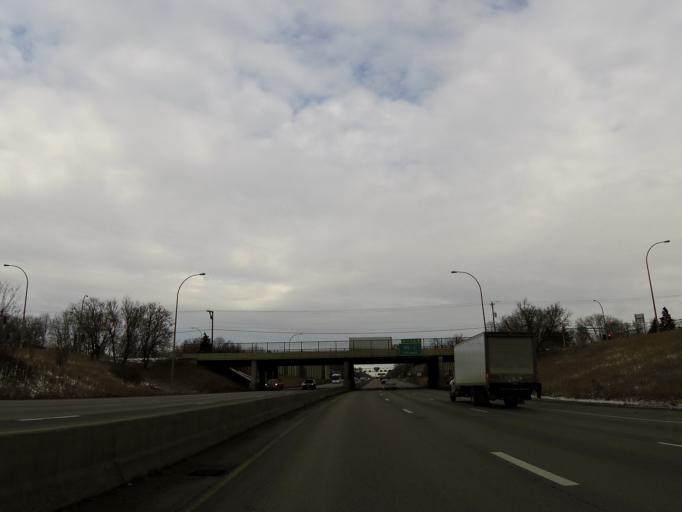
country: US
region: Minnesota
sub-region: Hennepin County
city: Bloomington
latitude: 44.8398
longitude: -93.2983
